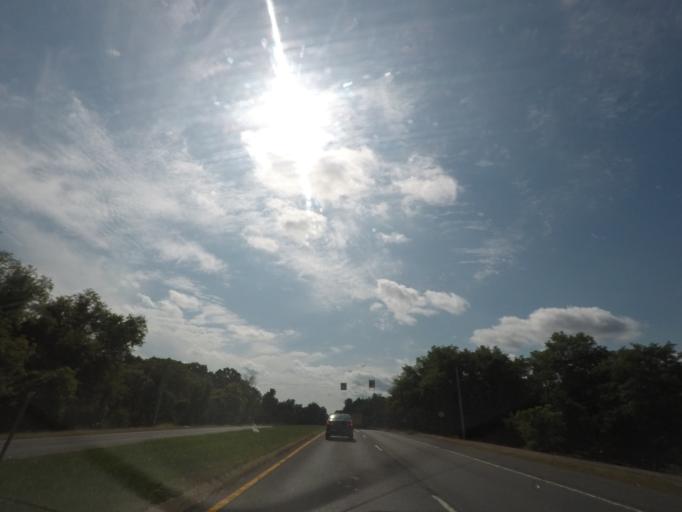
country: US
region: New York
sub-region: Albany County
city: Delmar
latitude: 42.6285
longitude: -73.8535
